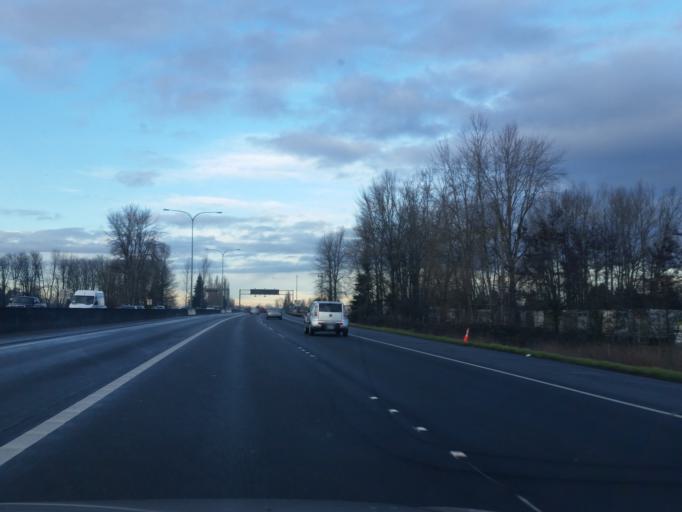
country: US
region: Washington
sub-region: King County
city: Kent
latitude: 47.3668
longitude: -122.2445
